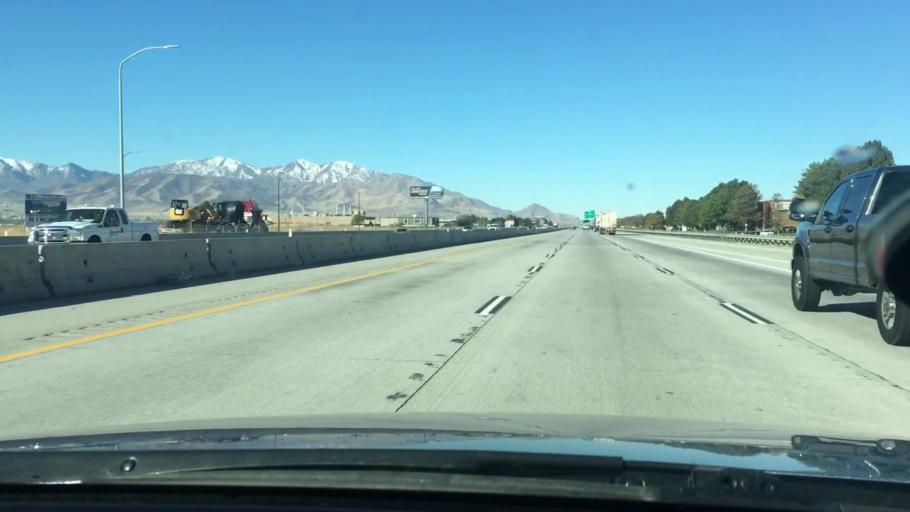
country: US
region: Utah
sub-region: Salt Lake County
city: West Valley City
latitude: 40.7259
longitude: -111.9933
